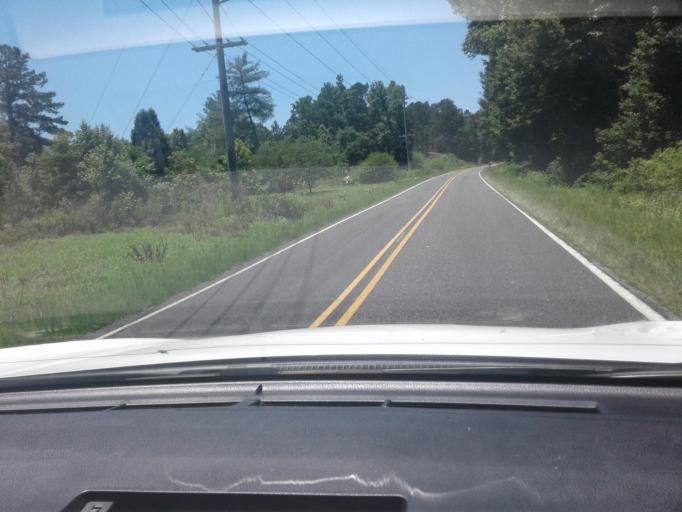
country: US
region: North Carolina
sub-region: Harnett County
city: Walkertown
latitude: 35.3382
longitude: -78.9036
